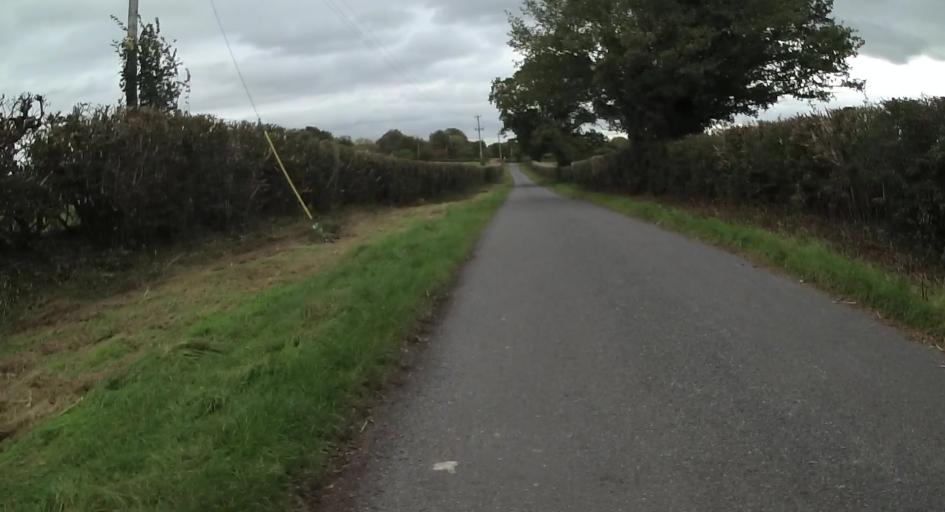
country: GB
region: England
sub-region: Hampshire
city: Four Marks
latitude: 51.1141
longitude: -1.0786
